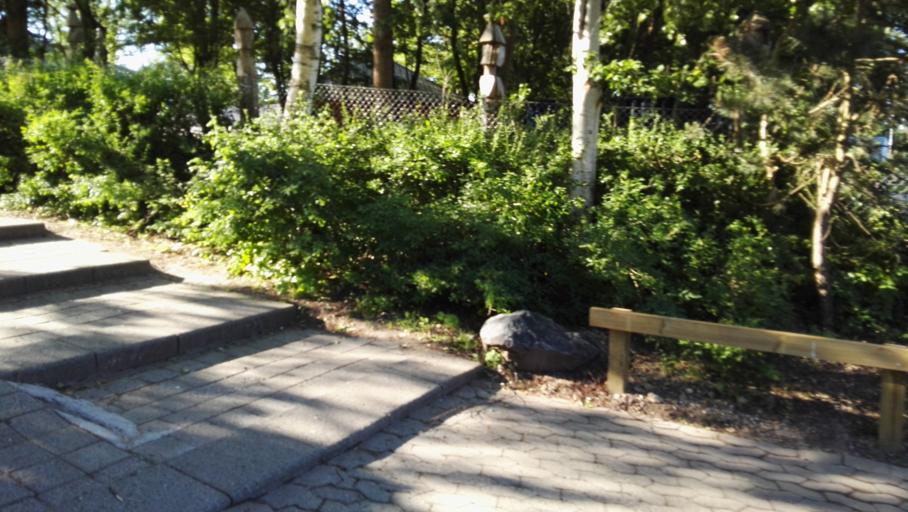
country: DK
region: Capital Region
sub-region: Ballerup Kommune
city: Ballerup
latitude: 55.7271
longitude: 12.3411
